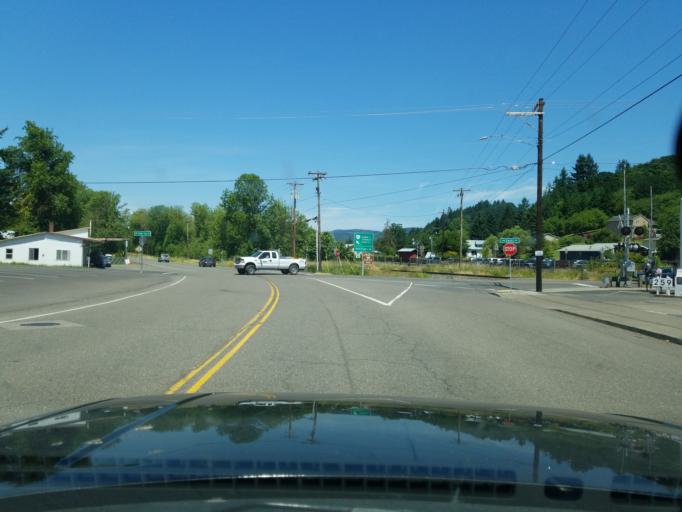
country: US
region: Oregon
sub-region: Washington County
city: Banks
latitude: 45.6214
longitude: -123.1144
